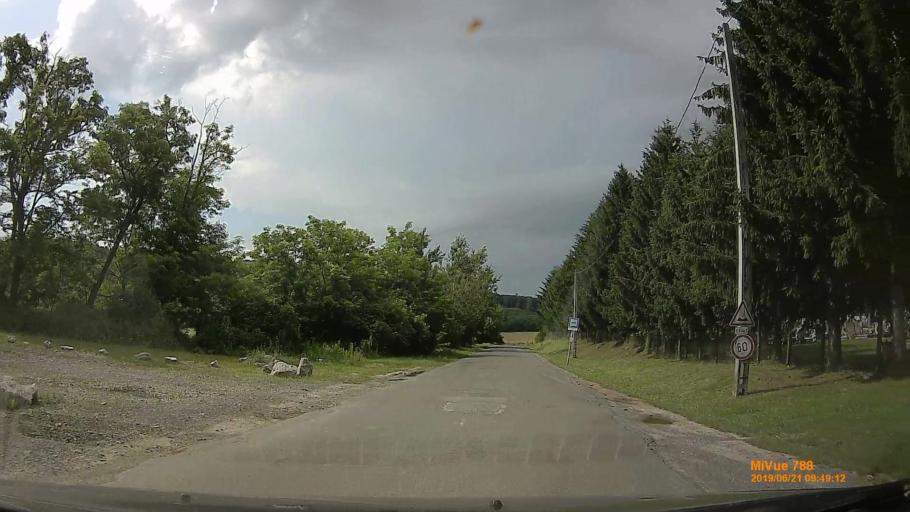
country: HU
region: Baranya
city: Sasd
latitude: 46.2696
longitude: 18.0384
